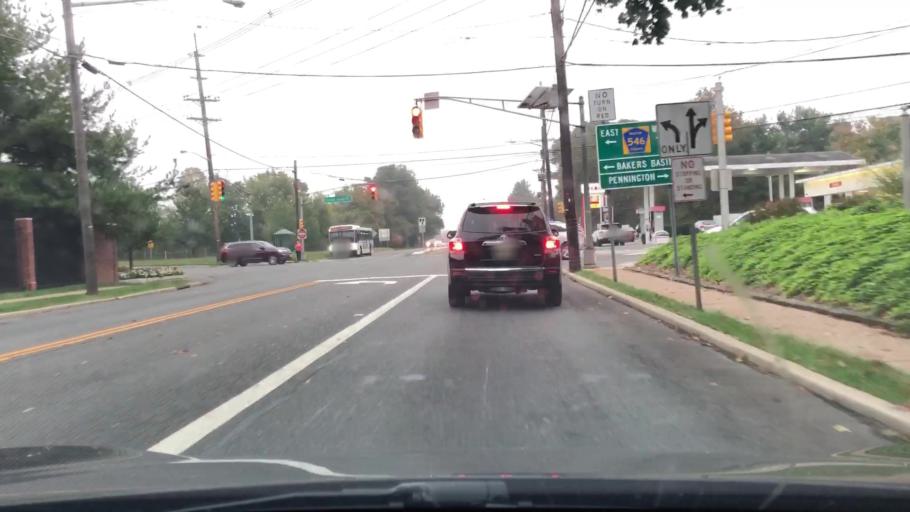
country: US
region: New Jersey
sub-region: Mercer County
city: Lawrenceville
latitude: 40.2904
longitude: -74.7339
